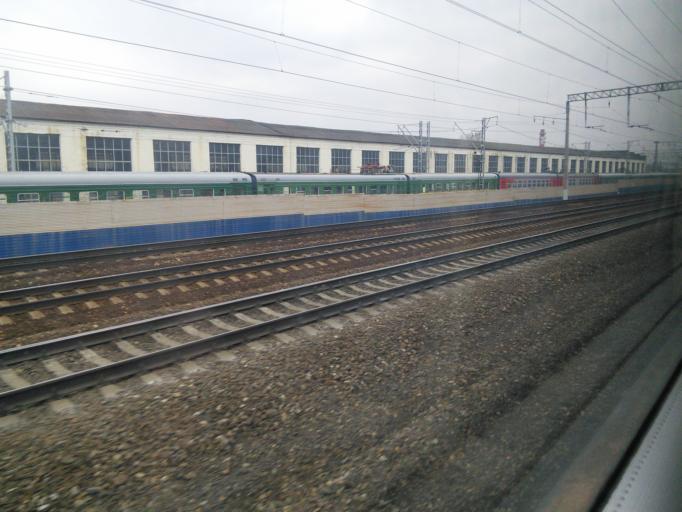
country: RU
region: Moskovskaya
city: Domodedovo
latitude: 55.4258
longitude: 37.7833
